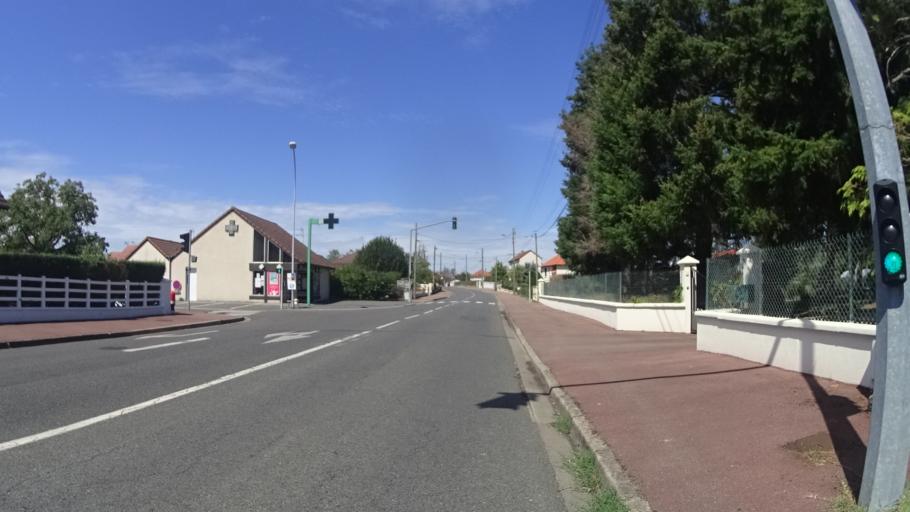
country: FR
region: Centre
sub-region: Departement du Loiret
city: Briare
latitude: 47.6261
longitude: 2.7498
